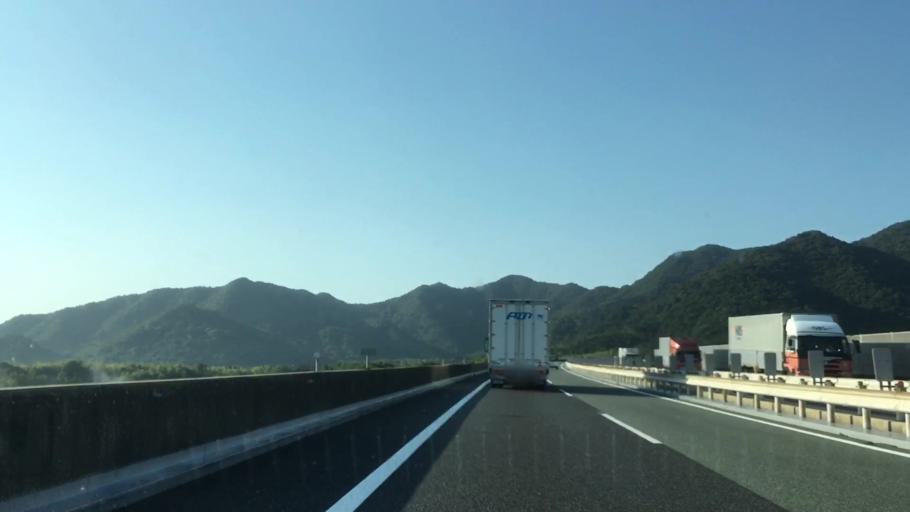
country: JP
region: Yamaguchi
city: Ogori-shimogo
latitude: 34.0930
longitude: 131.4561
